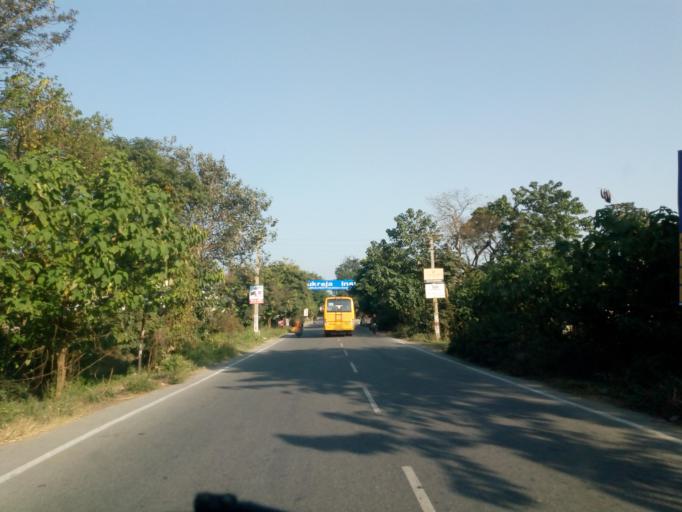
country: IN
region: Uttarakhand
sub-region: Dehradun
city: Dehradun
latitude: 30.3451
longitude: 77.9058
